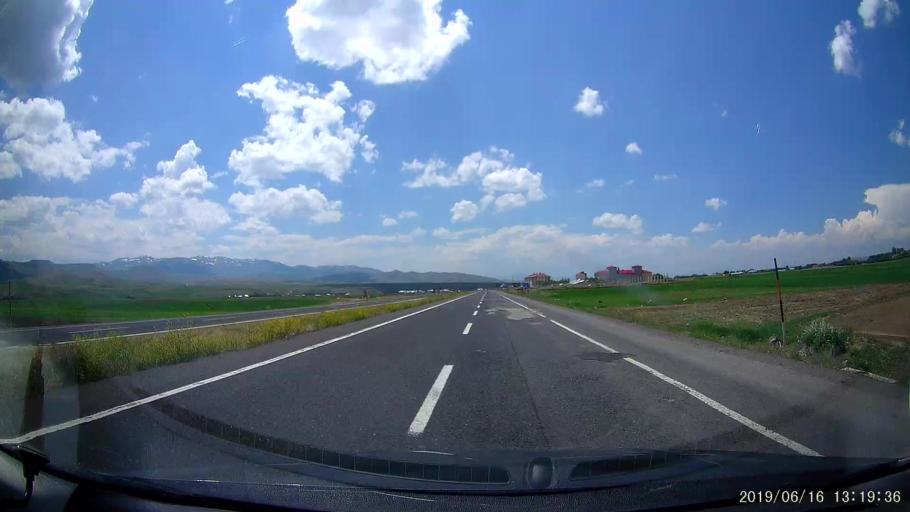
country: TR
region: Agri
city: Taslicay
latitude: 39.6328
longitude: 43.4027
